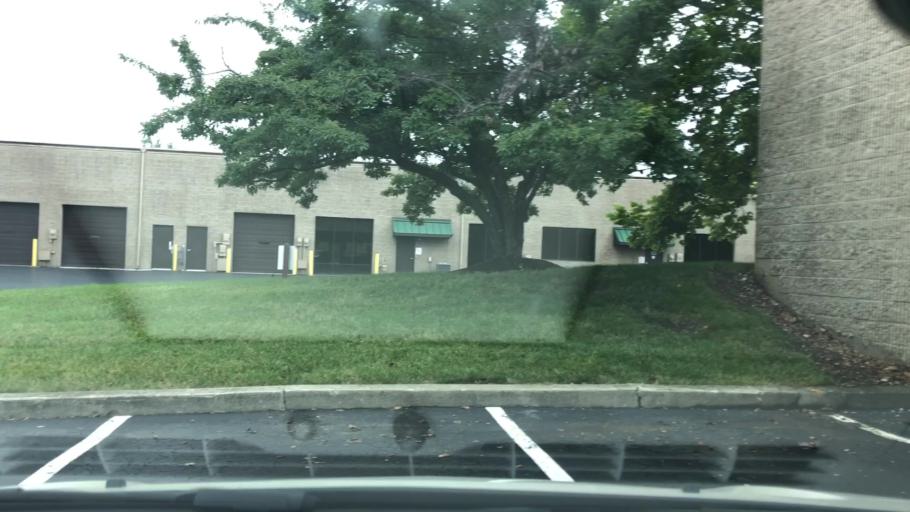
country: US
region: Ohio
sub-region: Franklin County
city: Worthington
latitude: 40.1102
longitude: -83.0017
